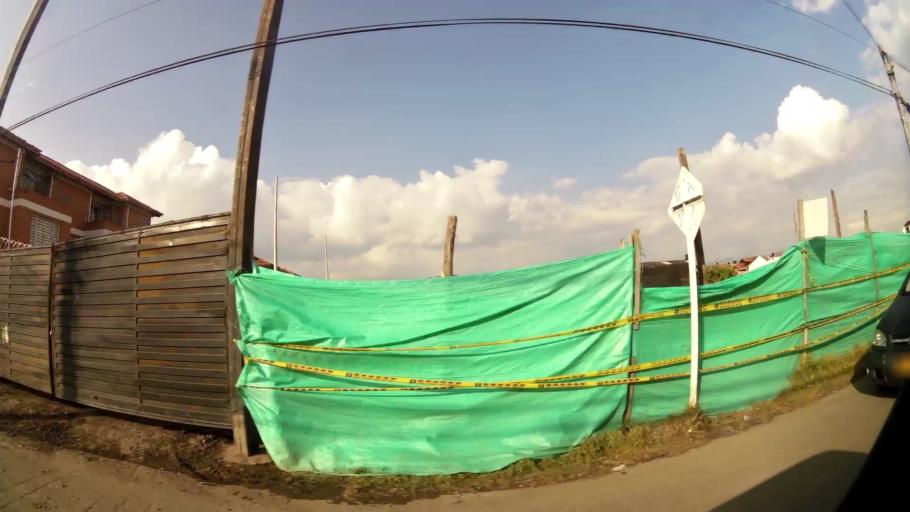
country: CO
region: Cundinamarca
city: Cota
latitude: 4.8098
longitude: -74.1064
